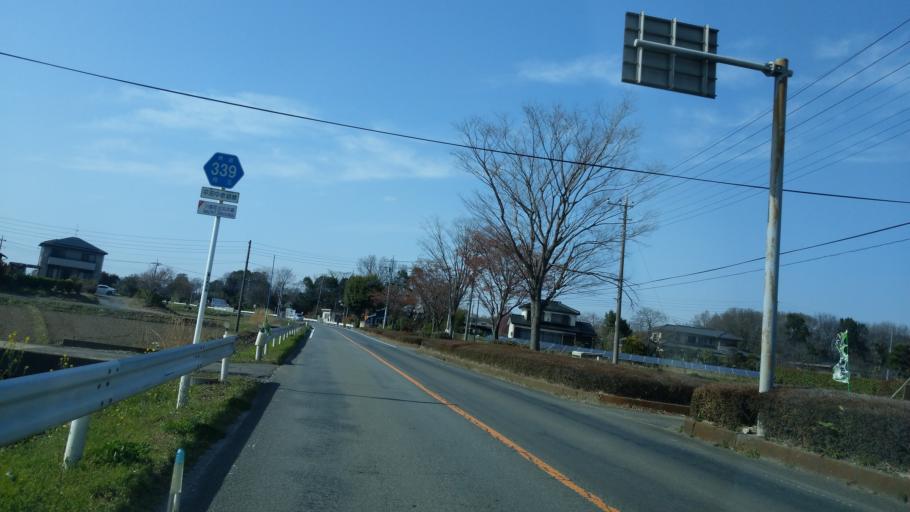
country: JP
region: Saitama
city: Okegawa
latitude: 35.9562
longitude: 139.5286
